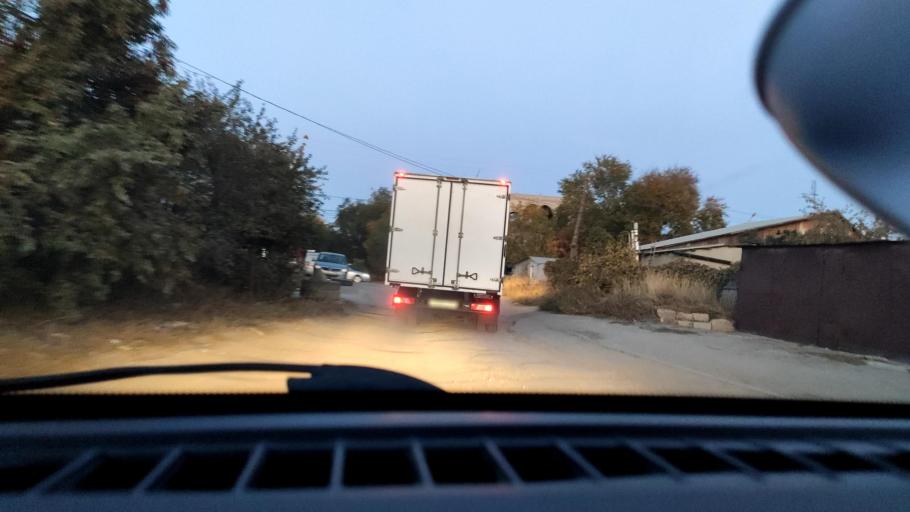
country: RU
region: Samara
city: Samara
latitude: 53.1781
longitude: 50.1678
